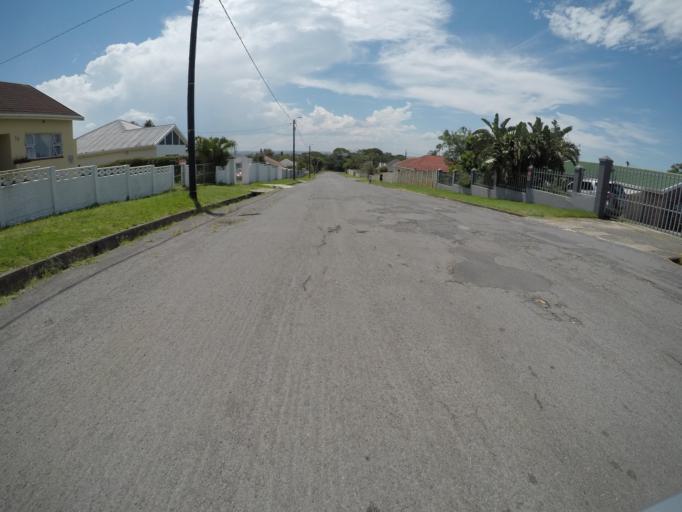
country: ZA
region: Eastern Cape
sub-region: Buffalo City Metropolitan Municipality
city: East London
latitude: -33.0342
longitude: 27.8562
